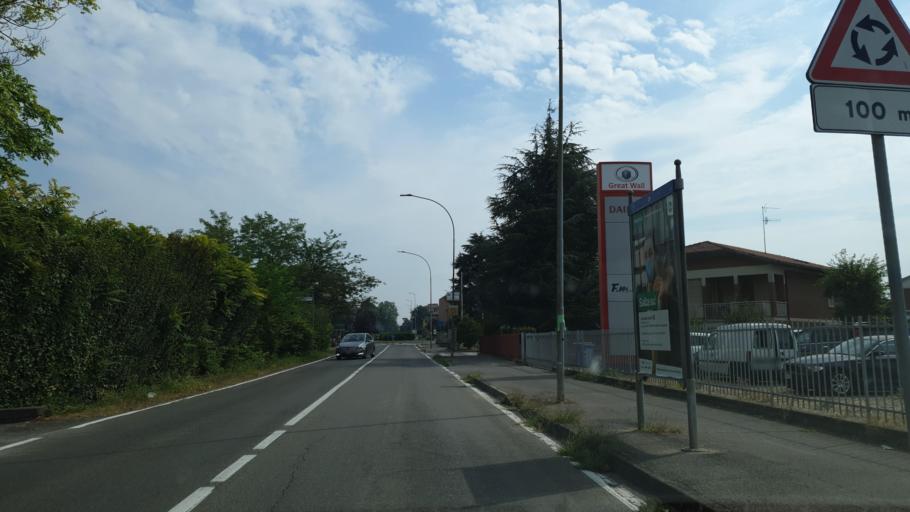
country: IT
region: Emilia-Romagna
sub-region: Provincia di Parma
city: Parma
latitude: 44.8132
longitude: 10.2917
